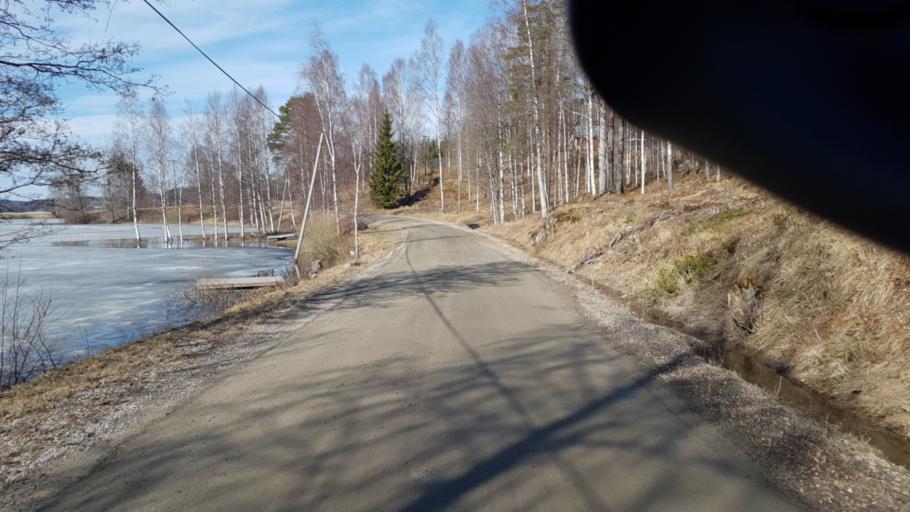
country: SE
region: Vaermland
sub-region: Arvika Kommun
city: Arvika
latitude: 59.7246
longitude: 12.8363
